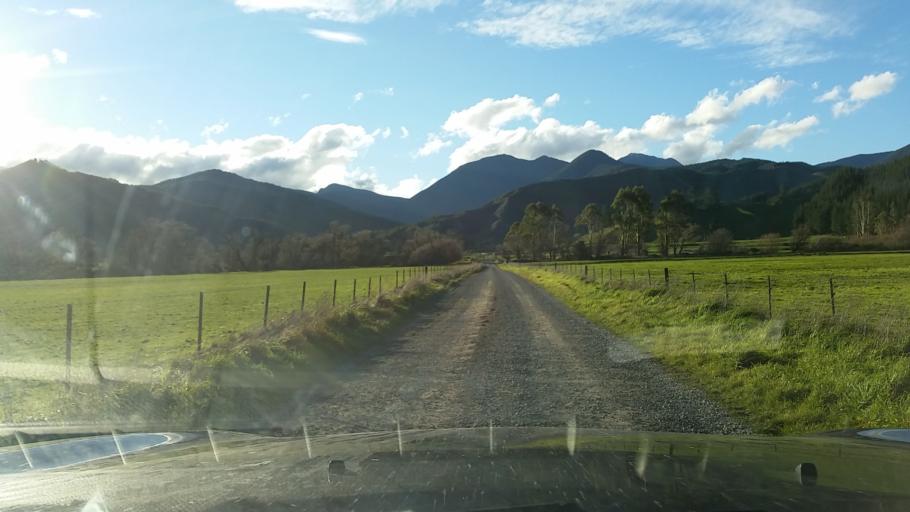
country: NZ
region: Nelson
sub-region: Nelson City
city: Nelson
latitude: -41.5472
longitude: 173.4987
